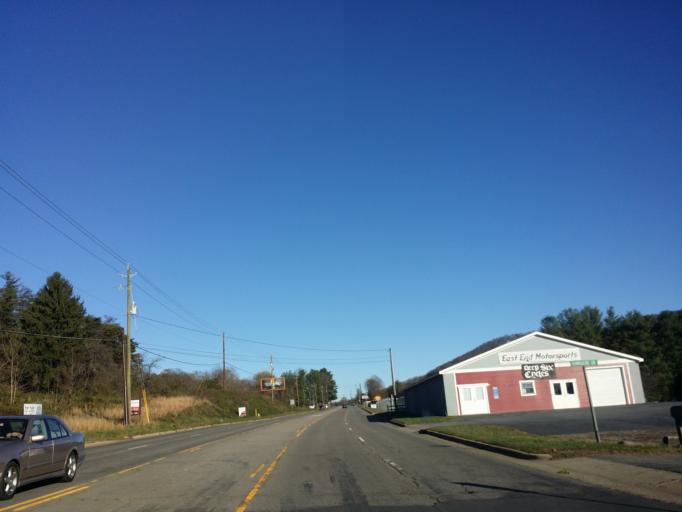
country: US
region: North Carolina
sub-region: Buncombe County
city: Swannanoa
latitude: 35.5930
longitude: -82.4358
